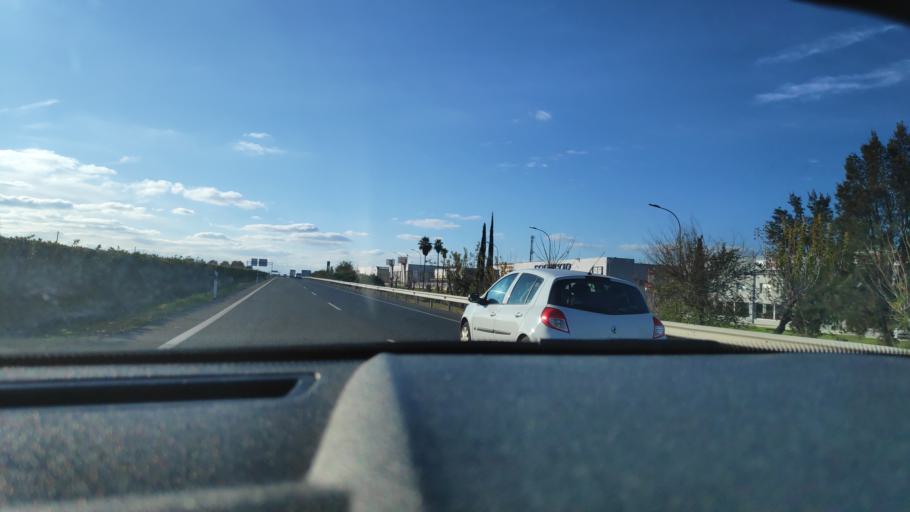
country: ES
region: Andalusia
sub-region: Provincia de Sevilla
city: Ecija
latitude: 37.5256
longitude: -5.1167
